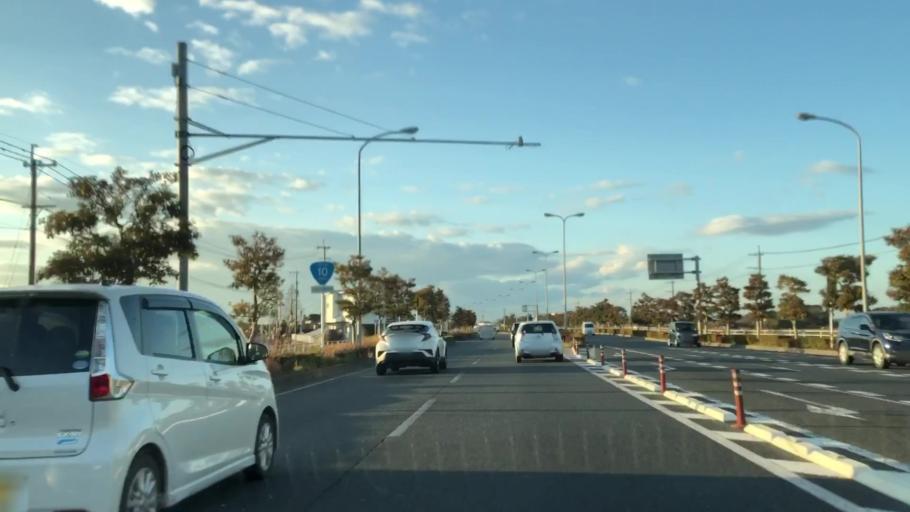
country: JP
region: Fukuoka
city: Nakatsu
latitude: 33.5430
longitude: 131.2879
